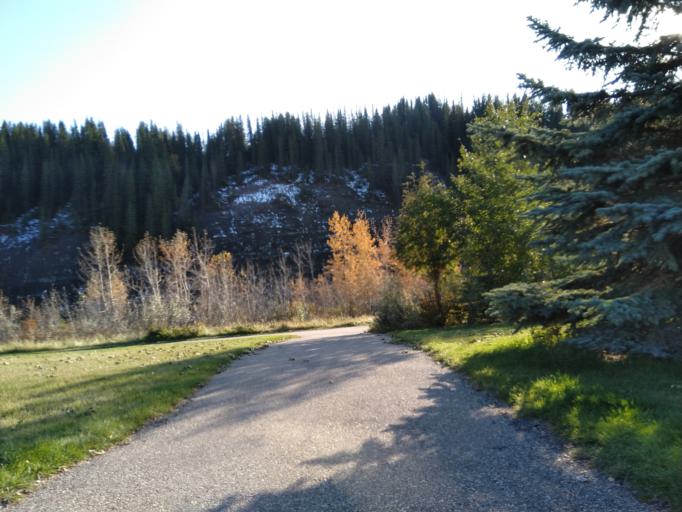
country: CA
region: Alberta
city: Cochrane
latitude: 51.1730
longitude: -114.4756
